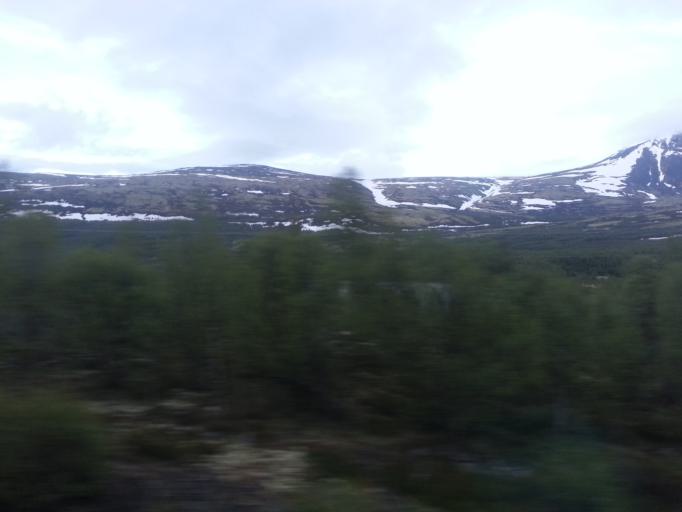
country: NO
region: Oppland
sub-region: Dovre
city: Dovre
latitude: 62.1761
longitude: 9.4481
